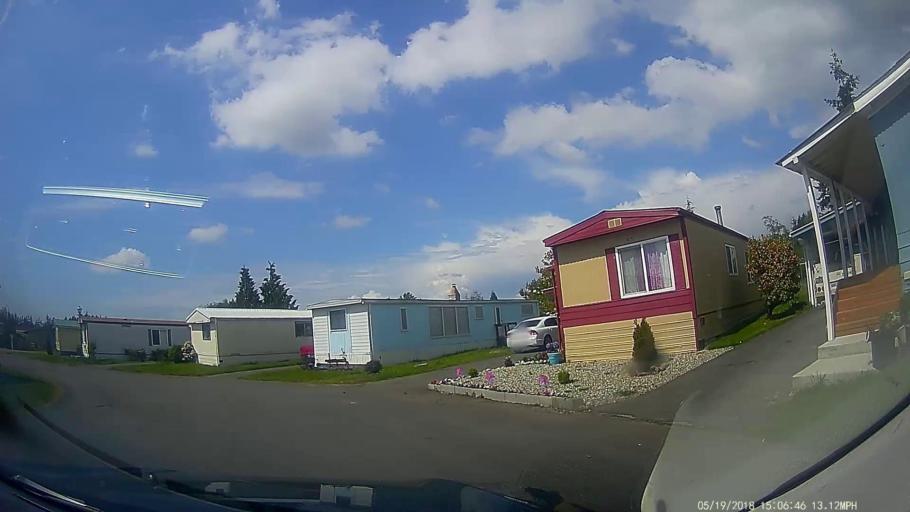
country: US
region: Washington
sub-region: Skagit County
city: Mount Vernon
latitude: 48.4157
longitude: -122.3070
